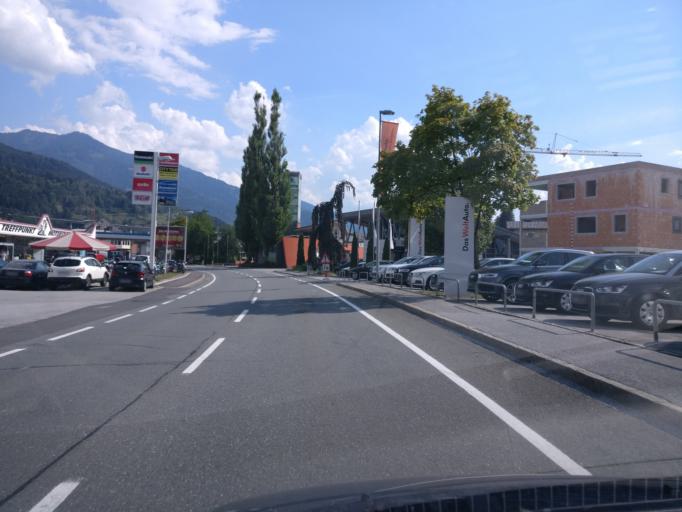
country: AT
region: Salzburg
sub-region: Politischer Bezirk Sankt Johann im Pongau
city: Bischofshofen
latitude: 47.4245
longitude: 13.2143
